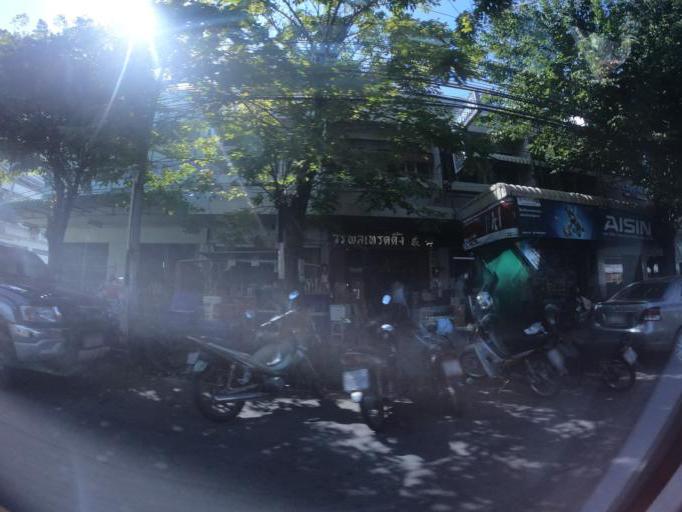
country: TH
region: Khon Kaen
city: Sam Sung
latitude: 16.4949
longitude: 102.9643
